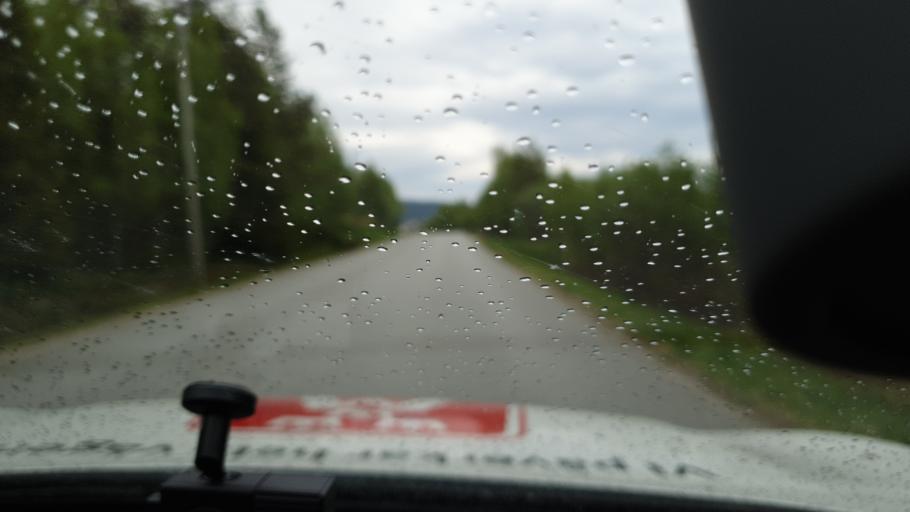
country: SE
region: Vaesterbotten
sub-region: Storumans Kommun
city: Fristad
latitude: 65.9572
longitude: 16.1982
